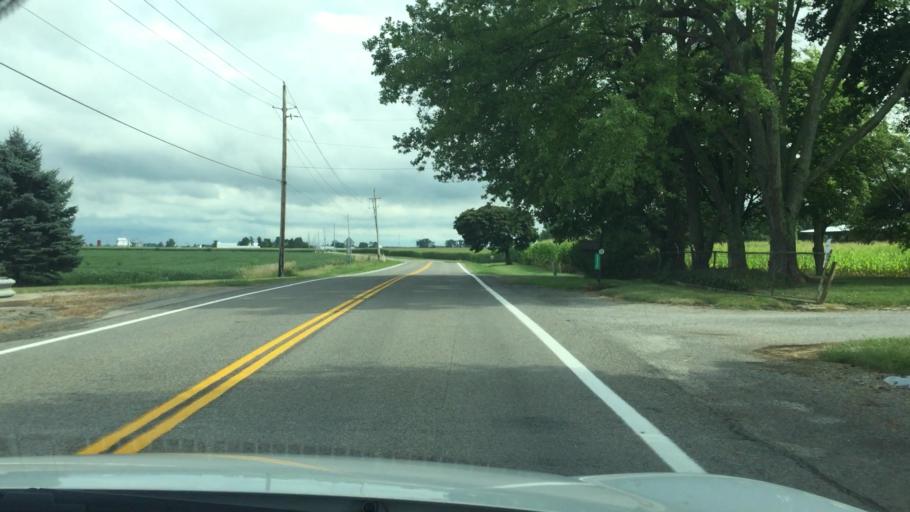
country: US
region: Ohio
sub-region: Champaign County
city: North Lewisburg
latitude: 40.2013
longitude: -83.5321
